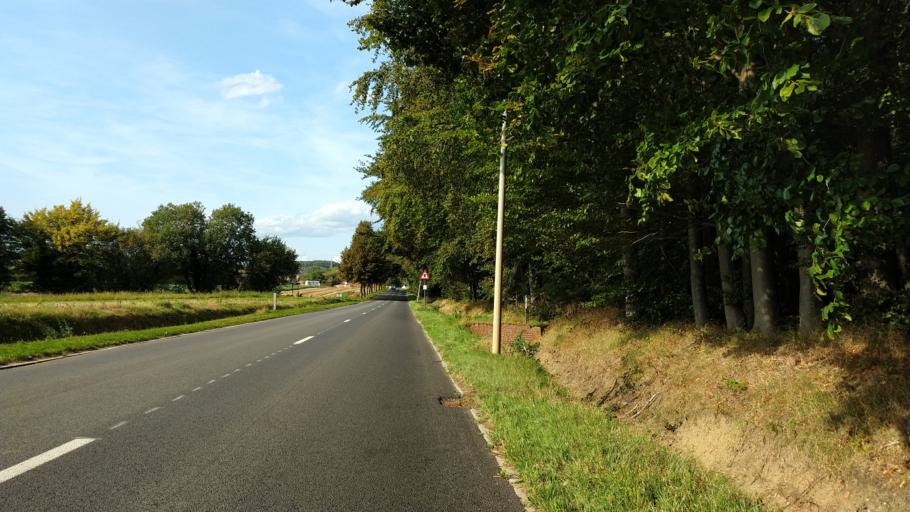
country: BE
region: Flanders
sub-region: Provincie Vlaams-Brabant
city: Boutersem
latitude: 50.8565
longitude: 4.8219
